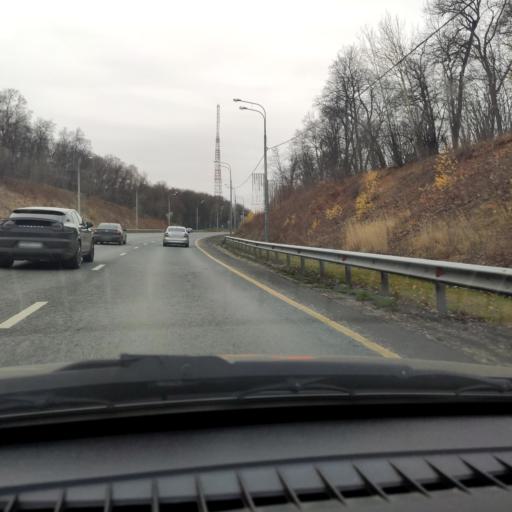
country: RU
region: Samara
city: Samara
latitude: 53.2996
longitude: 50.2261
